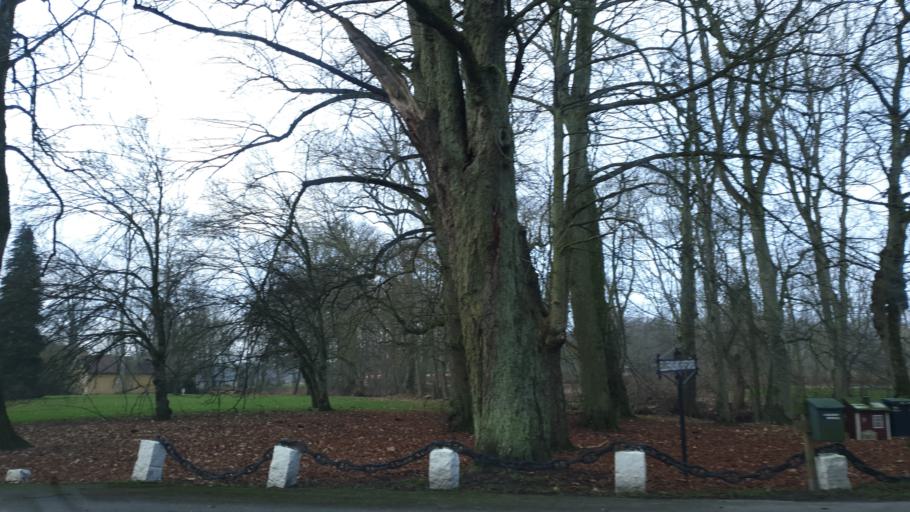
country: SE
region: Blekinge
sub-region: Karlshamns Kommun
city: Morrum
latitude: 56.1637
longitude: 14.7506
